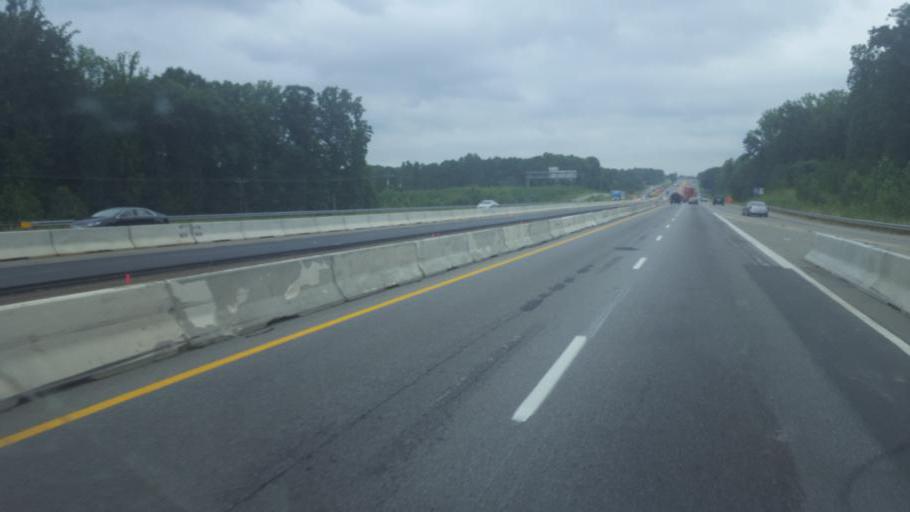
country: US
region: North Carolina
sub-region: Gaston County
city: Davidson
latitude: 35.5327
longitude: -80.8617
